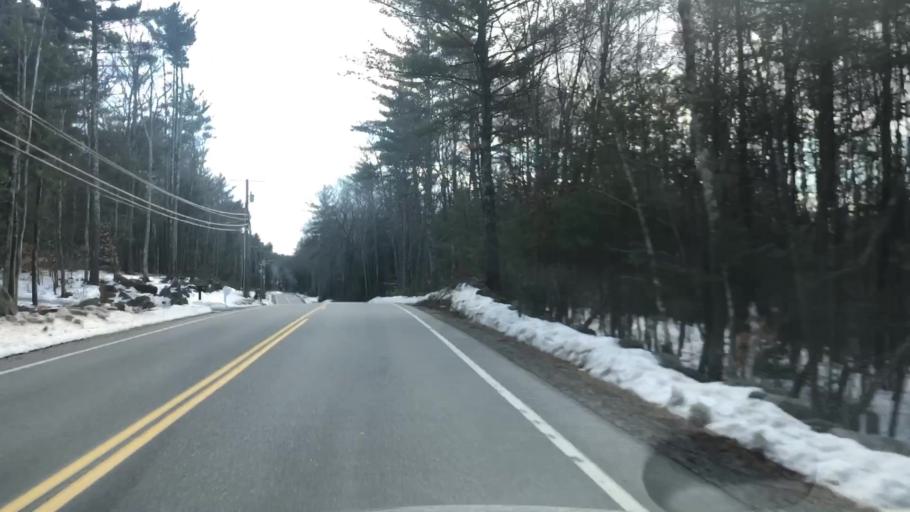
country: US
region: New Hampshire
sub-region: Hillsborough County
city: Mont Vernon
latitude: 42.8792
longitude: -71.6697
